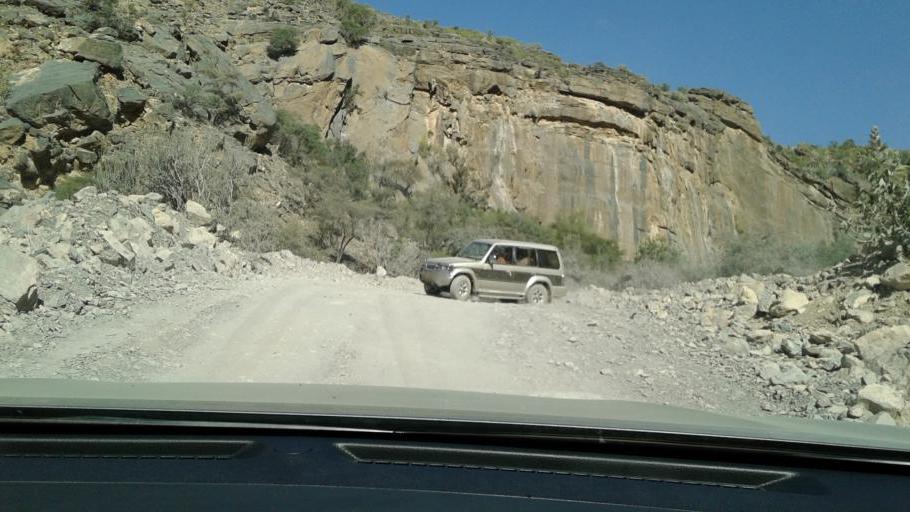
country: OM
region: Al Batinah
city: Bayt al `Awabi
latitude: 23.1729
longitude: 57.4232
